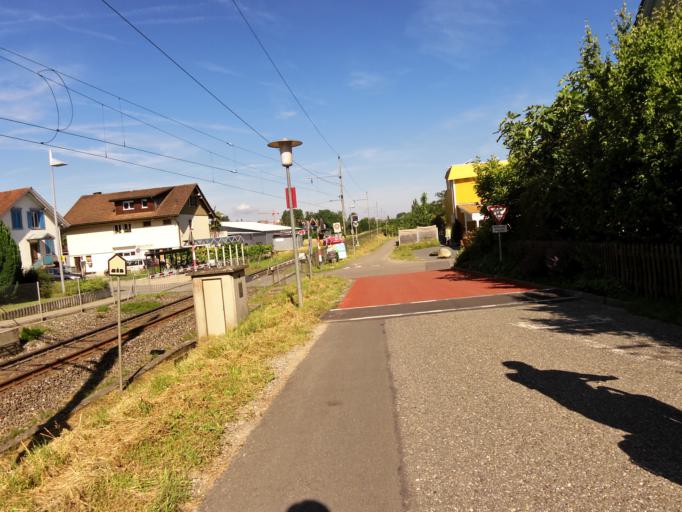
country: CH
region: Thurgau
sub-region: Kreuzlingen District
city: Munsterlingen
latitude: 47.6291
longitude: 9.2467
